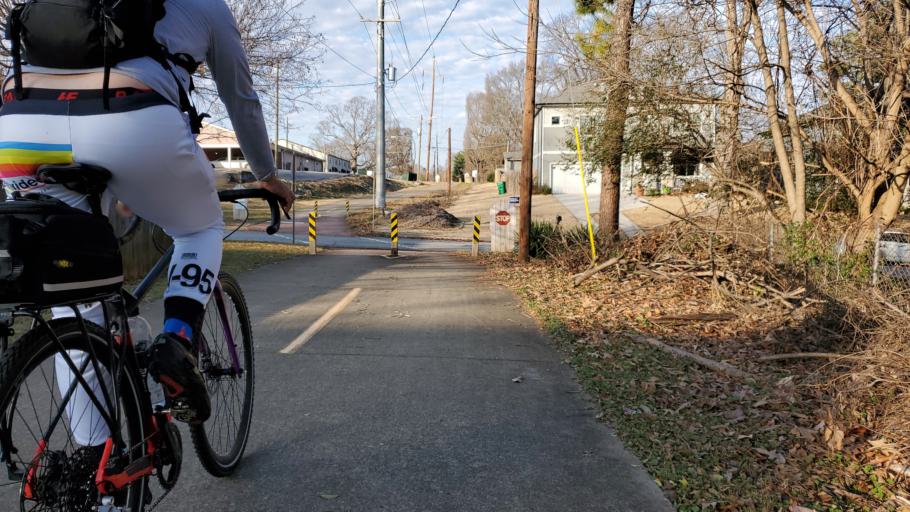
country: US
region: Georgia
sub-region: DeKalb County
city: Scottdale
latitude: 33.7843
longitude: -84.2626
